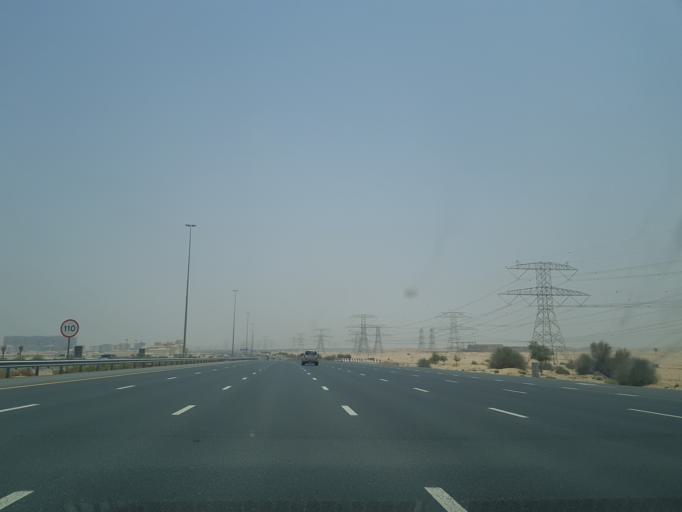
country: AE
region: Dubai
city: Dubai
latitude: 25.0707
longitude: 55.3638
